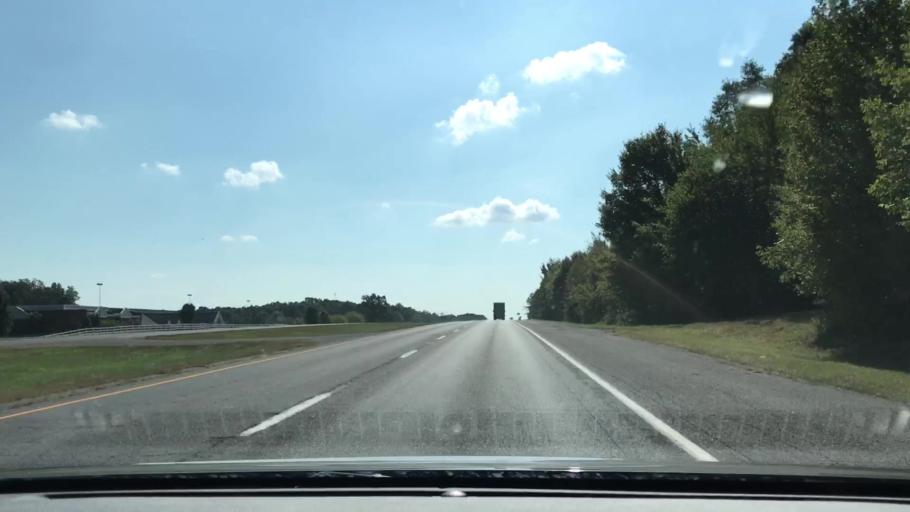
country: US
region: Kentucky
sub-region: Marshall County
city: Benton
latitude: 36.7717
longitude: -88.3163
